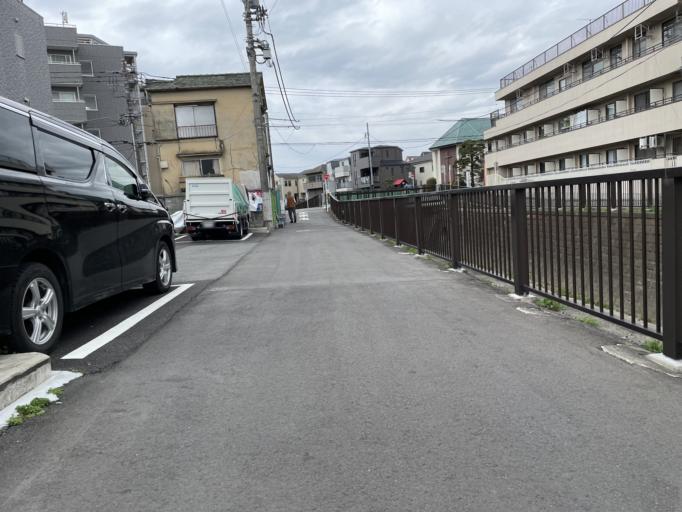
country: JP
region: Tokyo
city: Tokyo
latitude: 35.7158
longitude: 139.6480
